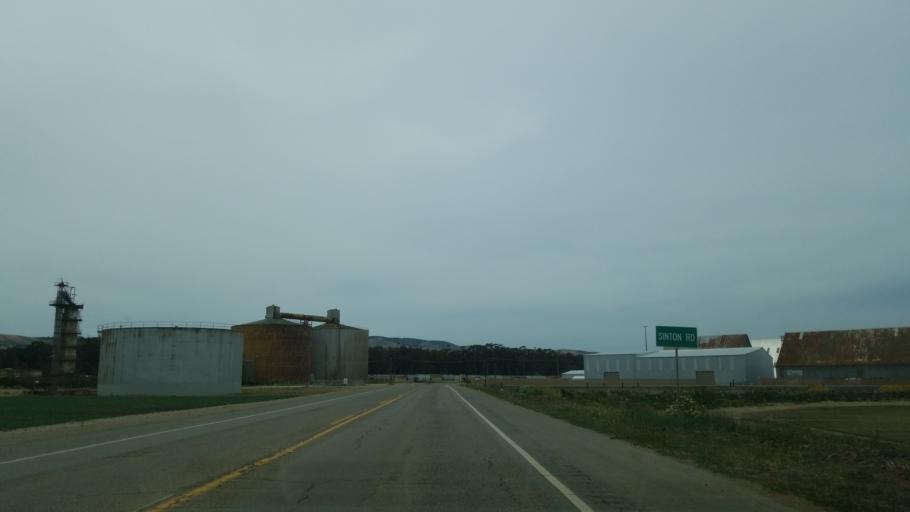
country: US
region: California
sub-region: Santa Barbara County
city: Guadalupe
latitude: 34.9185
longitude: -120.5127
